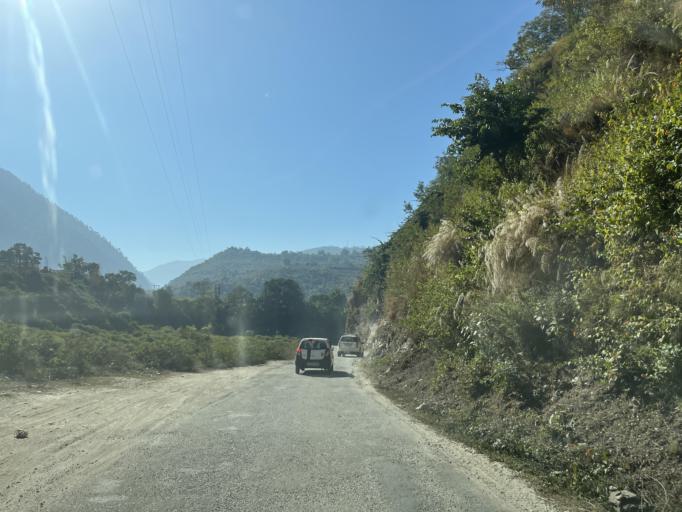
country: IN
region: Uttarakhand
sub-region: Naini Tal
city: Naini Tal
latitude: 29.5139
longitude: 79.4771
